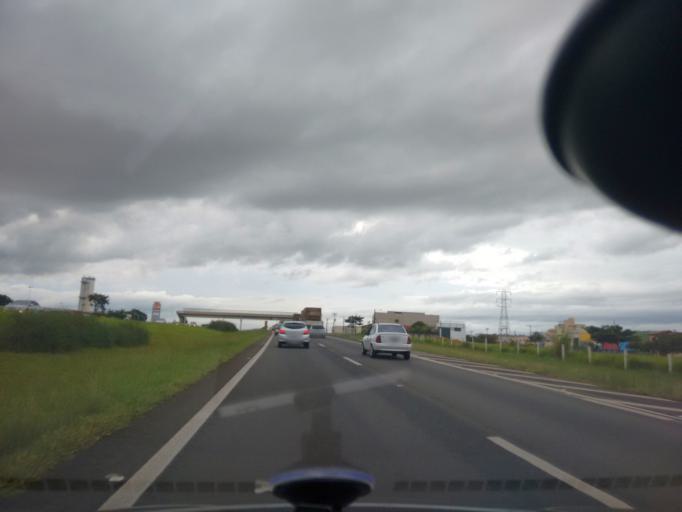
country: BR
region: Sao Paulo
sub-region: Rio Claro
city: Rio Claro
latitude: -22.4161
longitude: -47.5797
